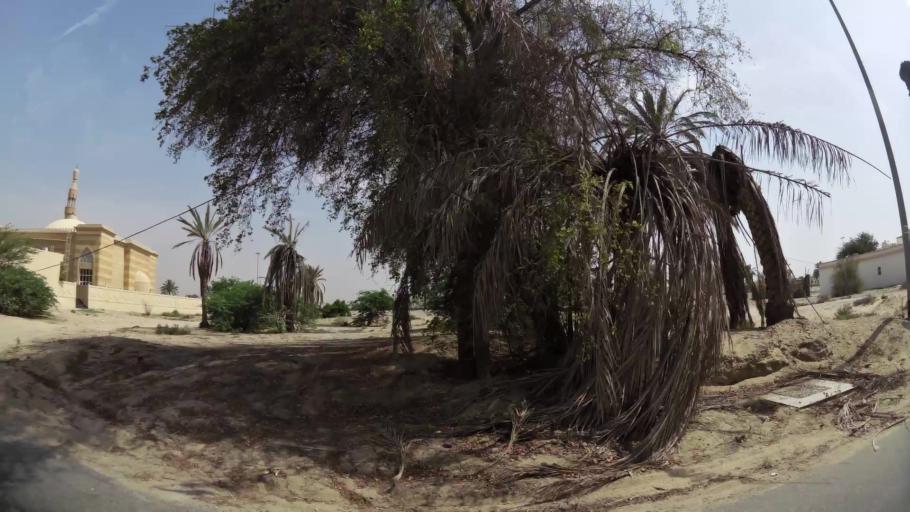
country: AE
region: Ash Shariqah
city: Sharjah
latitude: 25.2334
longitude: 55.4418
